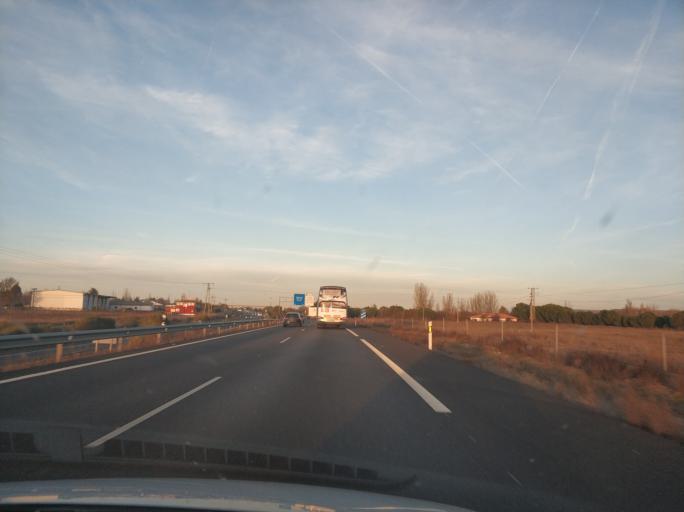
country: ES
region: Castille and Leon
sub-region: Provincia de Valladolid
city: Cubillas de Santa Marta
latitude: 41.8015
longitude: -4.5899
